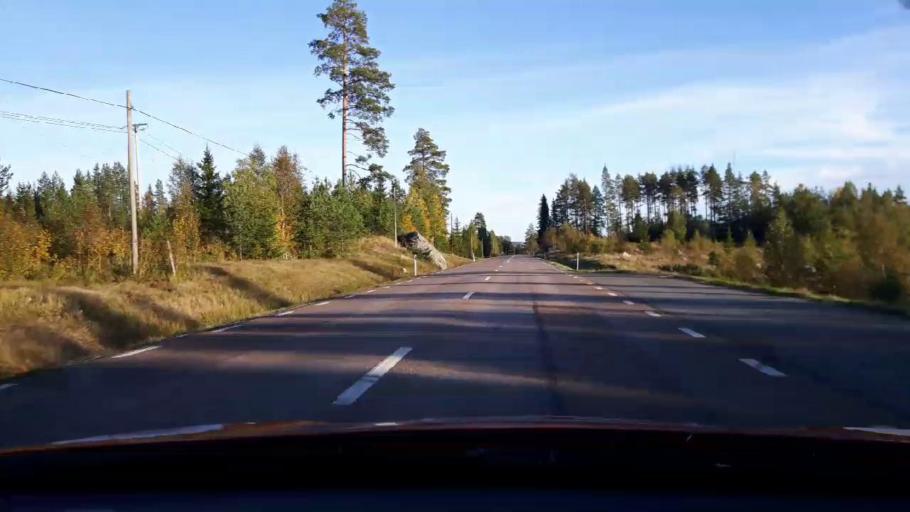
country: SE
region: Jaemtland
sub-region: OEstersunds Kommun
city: Brunflo
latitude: 62.9636
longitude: 15.0264
